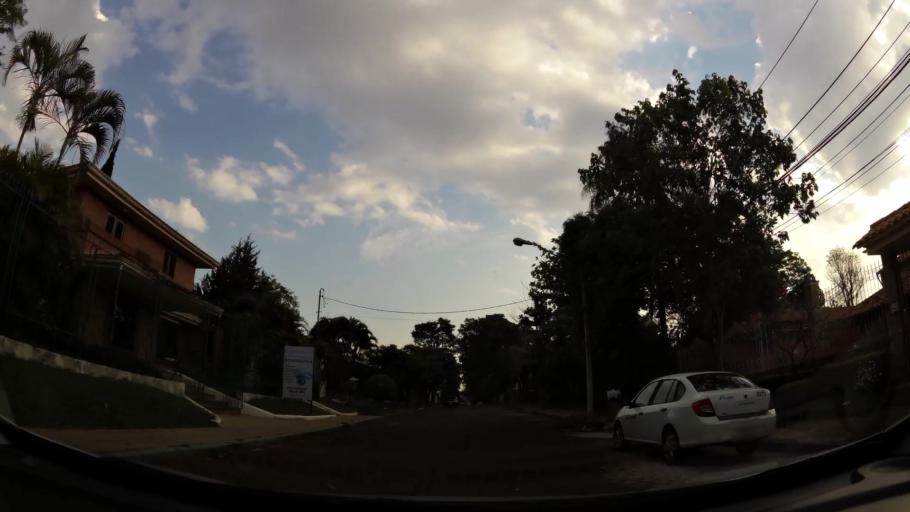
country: PY
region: Alto Parana
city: Presidente Franco
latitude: -25.5180
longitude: -54.6306
